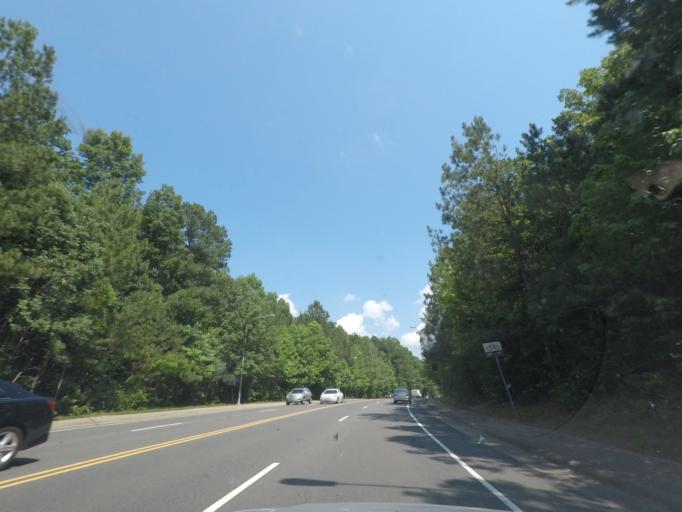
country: US
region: North Carolina
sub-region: Durham County
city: Durham
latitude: 35.9604
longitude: -78.9516
